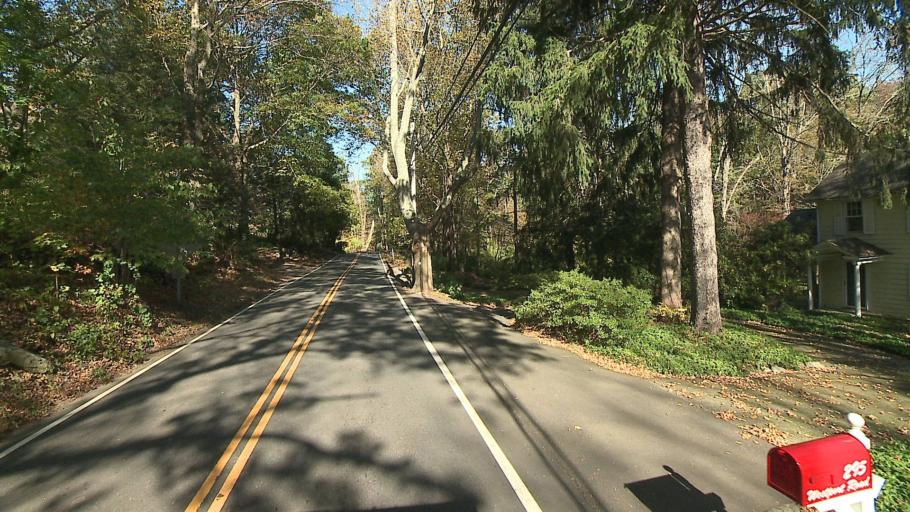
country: US
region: Connecticut
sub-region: Fairfield County
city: Trumbull
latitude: 41.2514
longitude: -73.3026
